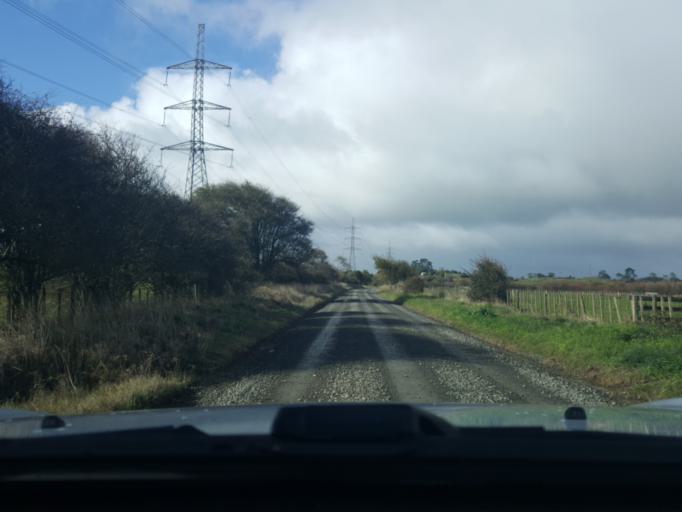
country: NZ
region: Waikato
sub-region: Waikato District
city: Te Kauwhata
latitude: -37.4179
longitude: 175.0679
